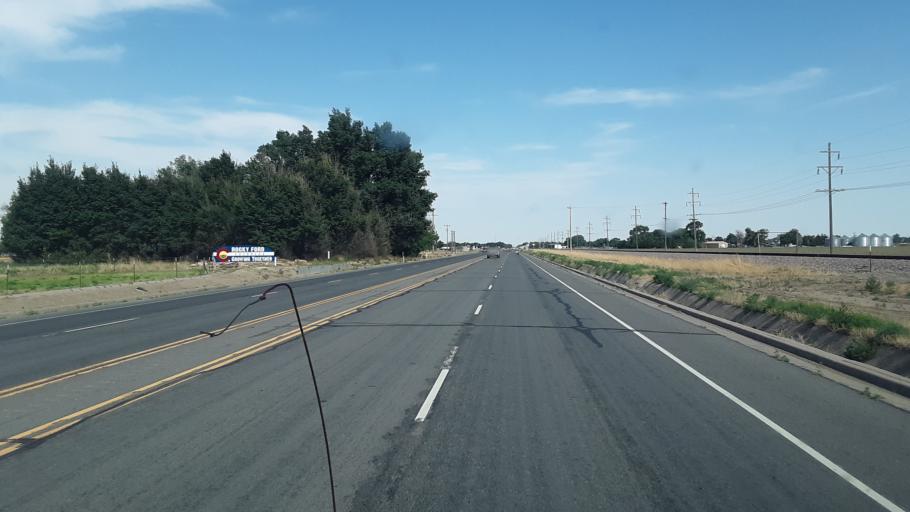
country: US
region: Colorado
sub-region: Otero County
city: Rocky Ford
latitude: 38.0668
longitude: -103.7542
